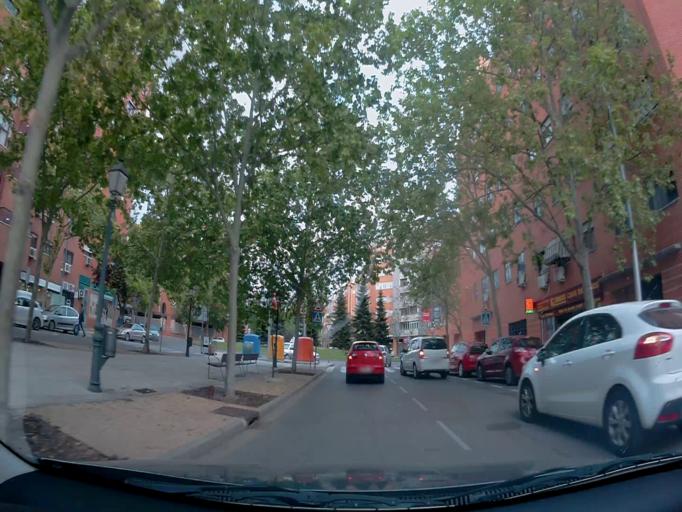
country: ES
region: Madrid
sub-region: Provincia de Madrid
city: Alcorcon
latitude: 40.3373
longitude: -3.8319
